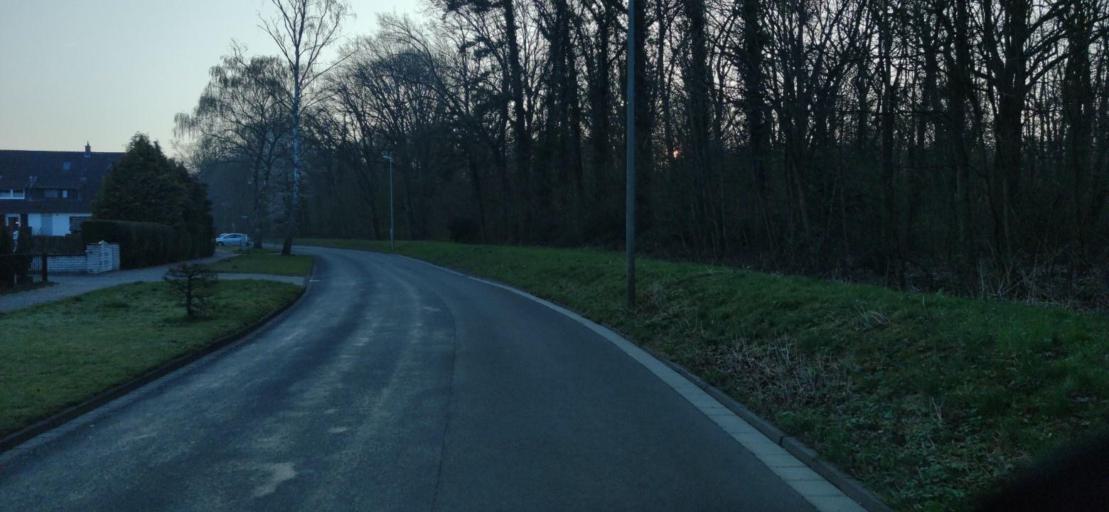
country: DE
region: North Rhine-Westphalia
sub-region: Regierungsbezirk Dusseldorf
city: Voerde
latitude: 51.5763
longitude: 6.6932
